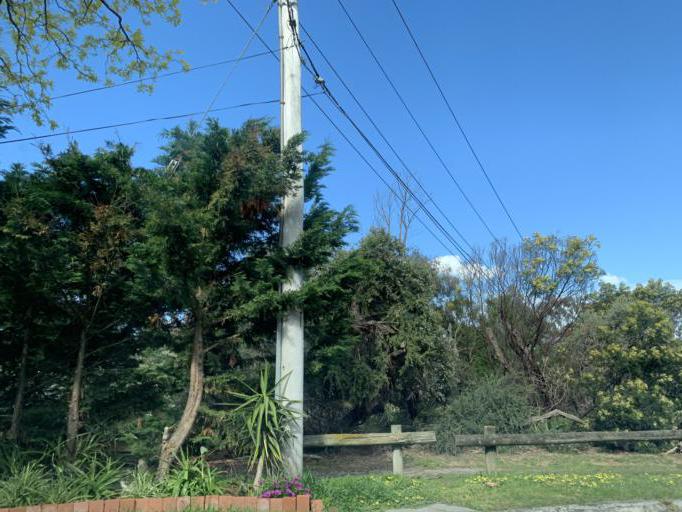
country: AU
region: Victoria
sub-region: Bayside
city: Highett
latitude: -37.9614
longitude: 145.0278
